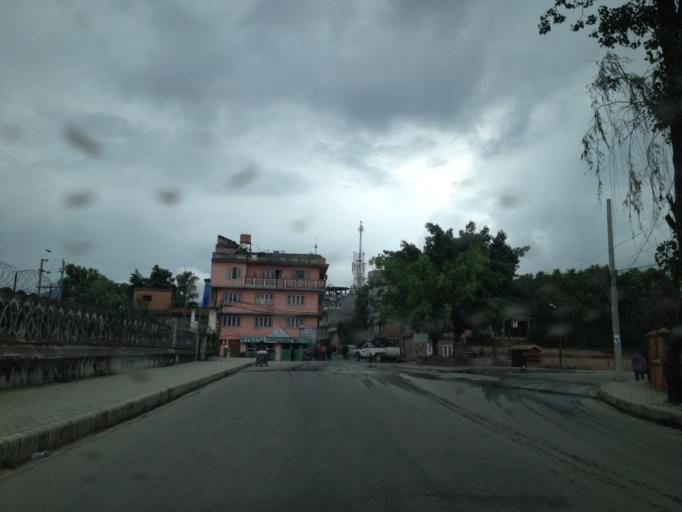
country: NP
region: Central Region
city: Kirtipur
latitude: 27.7061
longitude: 85.2890
